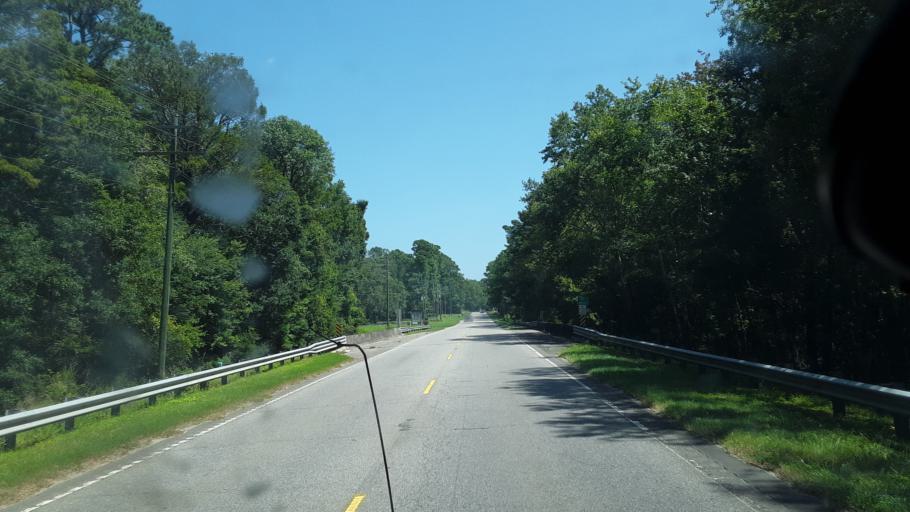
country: US
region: South Carolina
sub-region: Horry County
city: Forestbrook
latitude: 33.8328
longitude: -78.8863
